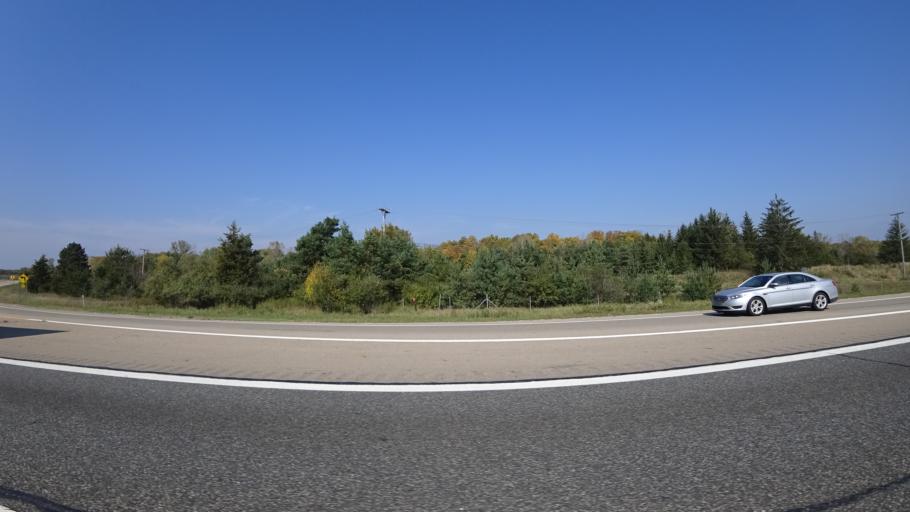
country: US
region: Michigan
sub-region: Washtenaw County
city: Chelsea
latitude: 42.2982
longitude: -83.9711
